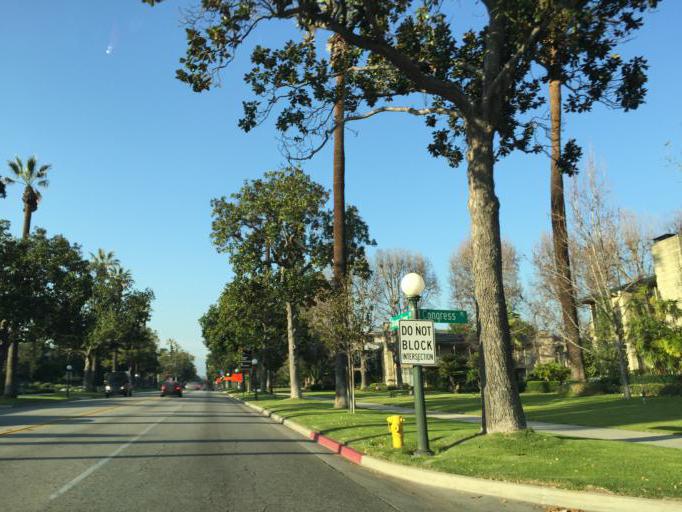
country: US
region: California
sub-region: Los Angeles County
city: South Pasadena
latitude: 34.1339
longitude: -118.1588
